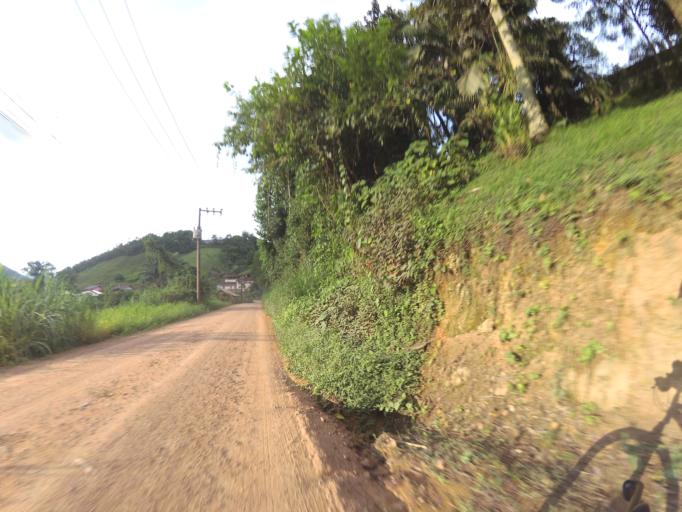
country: BR
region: Santa Catarina
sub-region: Pomerode
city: Pomerode
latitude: -26.7570
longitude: -49.1655
